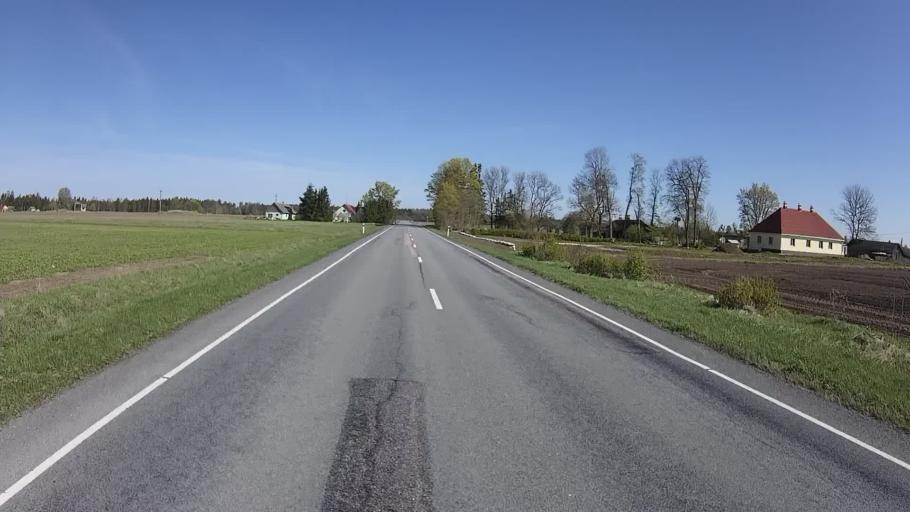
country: EE
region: Raplamaa
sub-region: Jaervakandi vald
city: Jarvakandi
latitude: 58.8409
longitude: 24.7966
